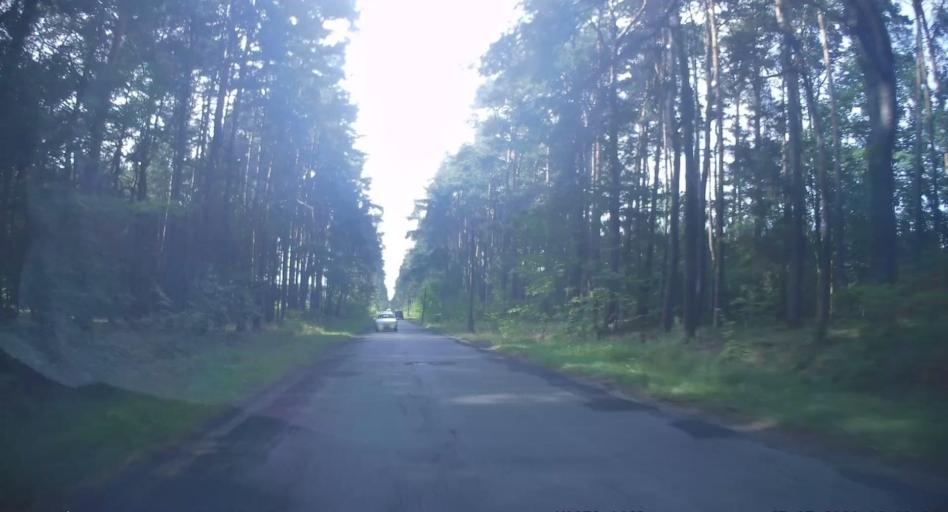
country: PL
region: Swietokrzyskie
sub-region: Powiat konecki
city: Konskie
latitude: 51.2202
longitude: 20.3888
